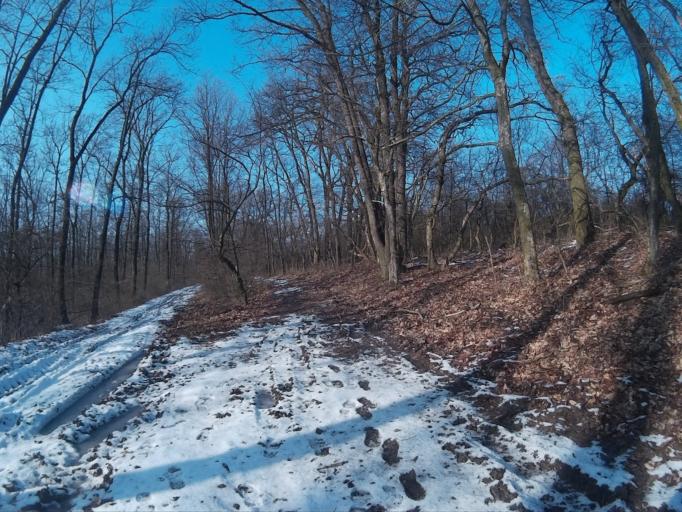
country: HU
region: Komarom-Esztergom
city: Labatlan
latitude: 47.7237
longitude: 18.4879
